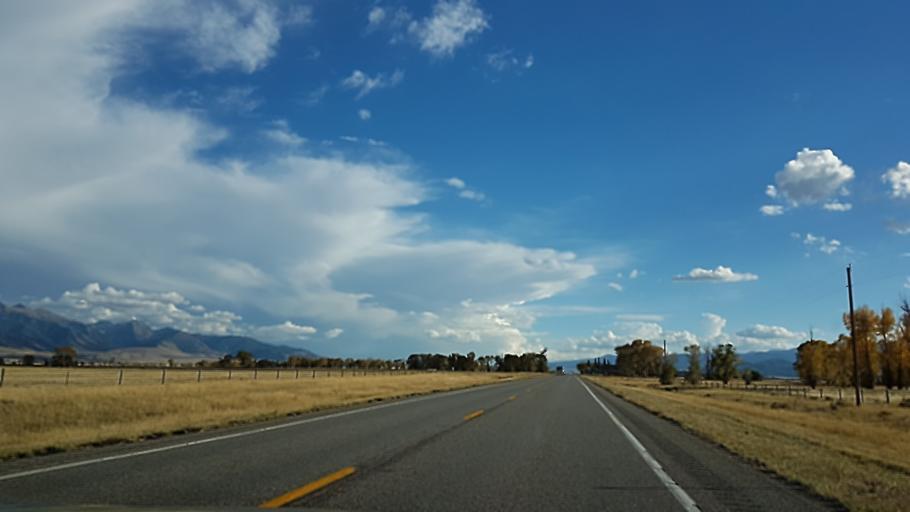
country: US
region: Montana
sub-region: Madison County
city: Virginia City
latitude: 45.2087
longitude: -111.6788
